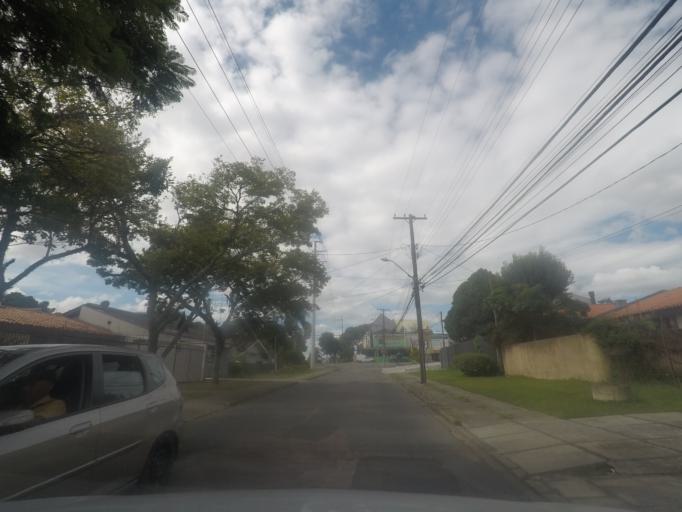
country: BR
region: Parana
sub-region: Pinhais
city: Pinhais
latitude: -25.4609
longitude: -49.2244
